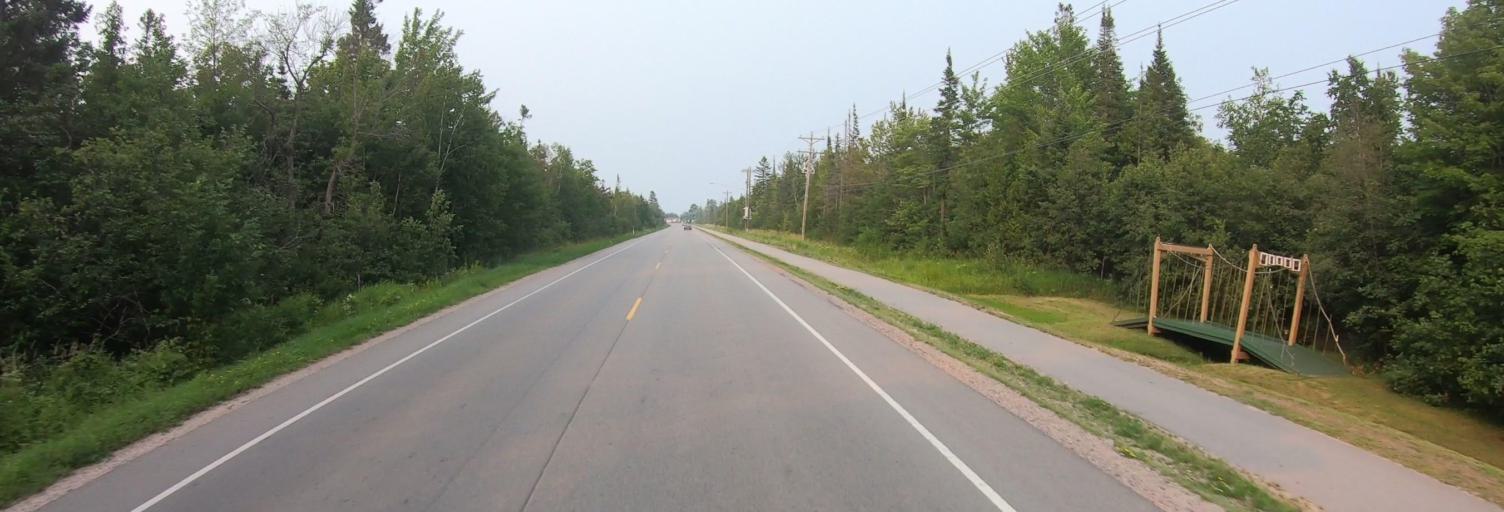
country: US
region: Michigan
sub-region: Chippewa County
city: Sault Ste. Marie
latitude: 46.4420
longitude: -84.6039
